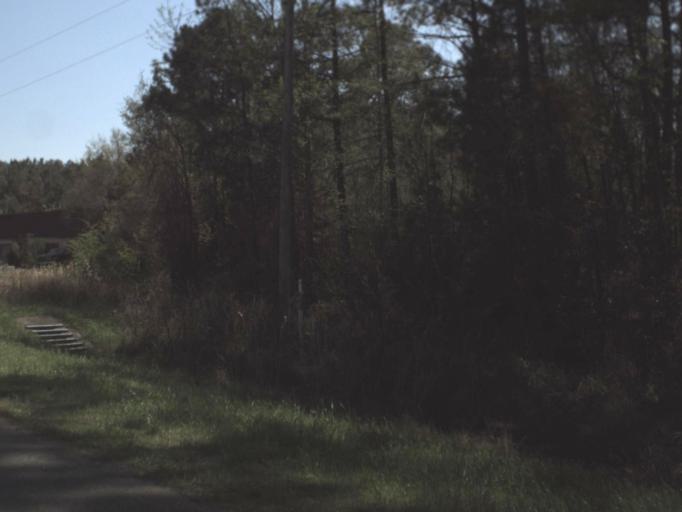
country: US
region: Florida
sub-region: Calhoun County
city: Blountstown
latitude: 30.4282
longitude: -85.1676
